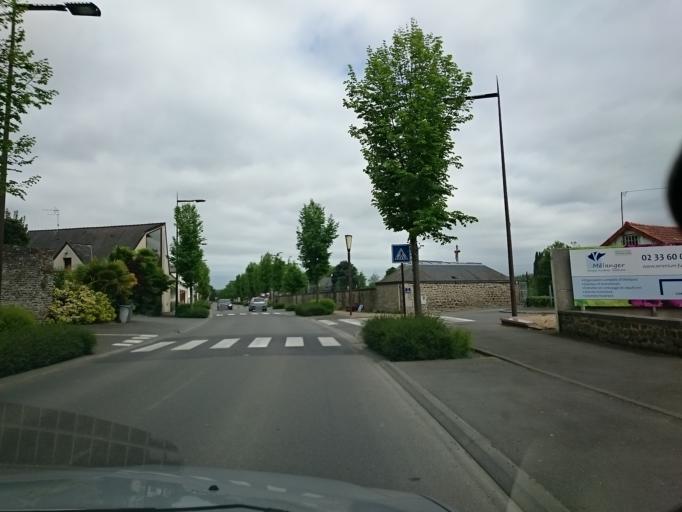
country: FR
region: Lower Normandy
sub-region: Departement de la Manche
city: Pontorson
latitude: 48.5542
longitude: -1.5064
